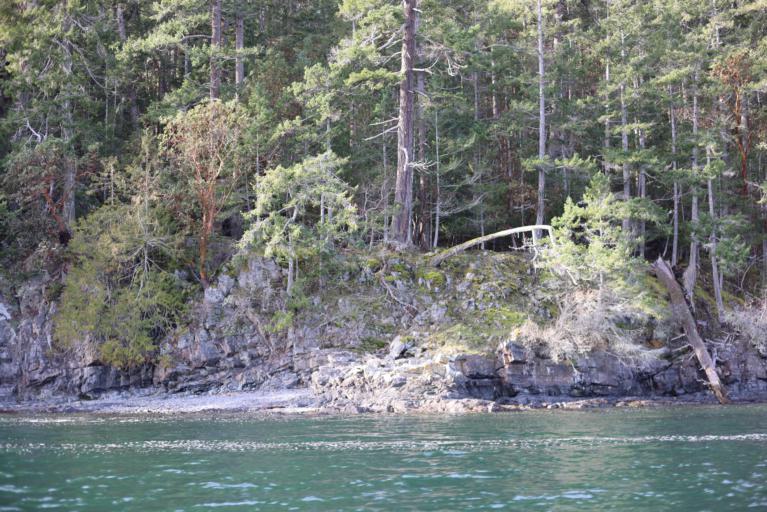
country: CA
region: British Columbia
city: Duncan
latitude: 48.7606
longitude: -123.5779
